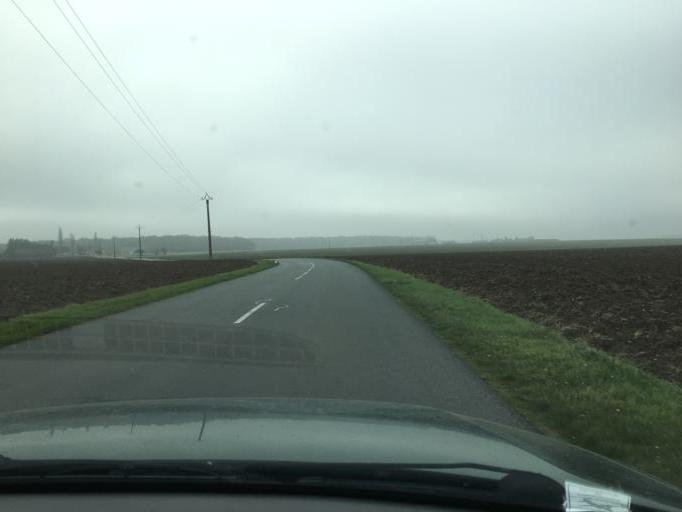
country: FR
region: Centre
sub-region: Departement du Loiret
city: Gidy
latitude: 47.9731
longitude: 1.8396
